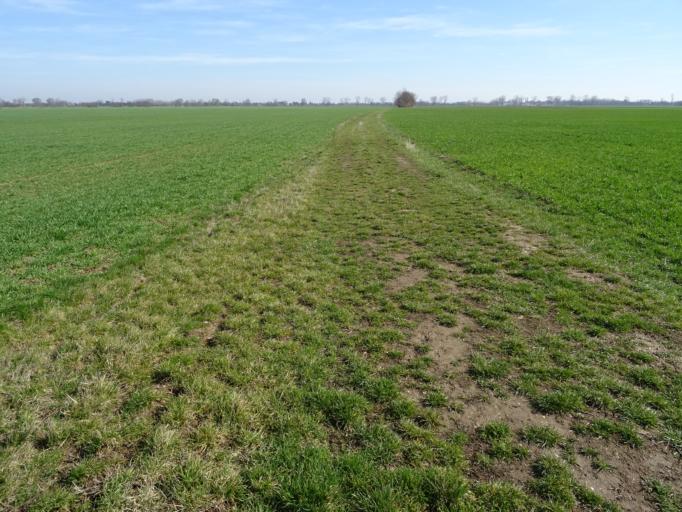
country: HU
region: Gyor-Moson-Sopron
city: Mihalyi
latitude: 47.5139
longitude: 17.0615
